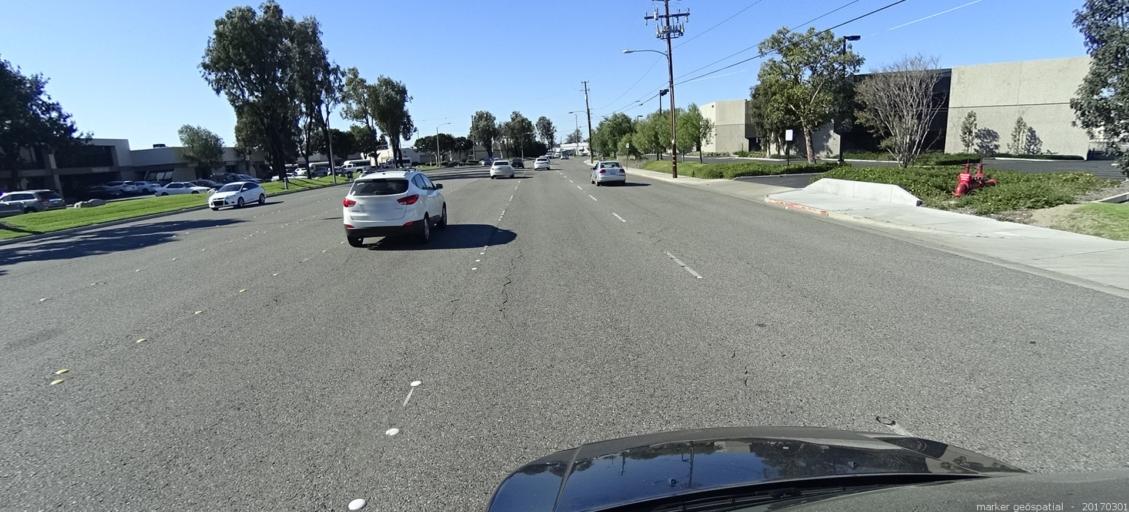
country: US
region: California
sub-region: Orange County
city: Placentia
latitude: 33.8605
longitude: -117.8402
